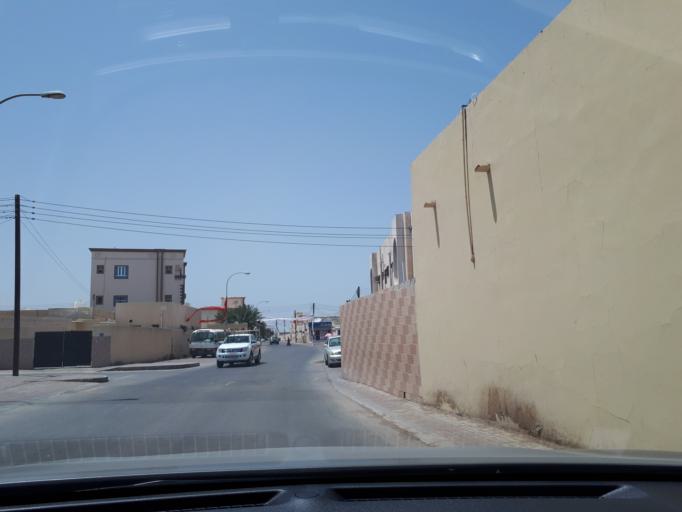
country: OM
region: Muhafazat Masqat
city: As Sib al Jadidah
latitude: 23.6801
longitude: 58.1257
